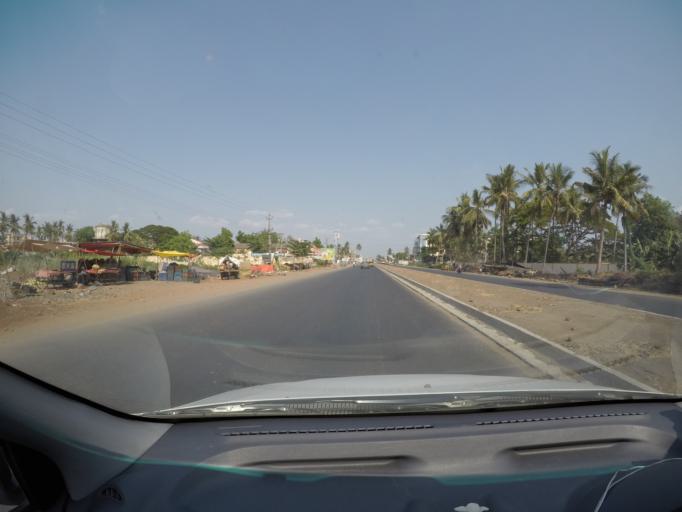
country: IN
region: Andhra Pradesh
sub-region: Krishna
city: Yanamalakuduru
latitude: 16.4745
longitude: 80.7118
